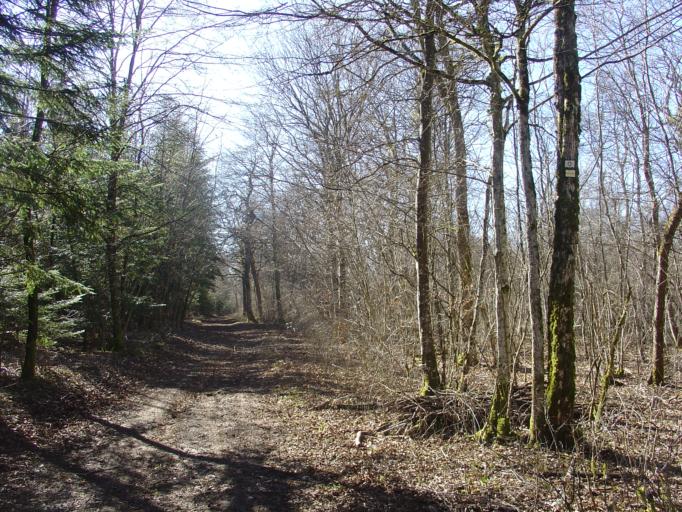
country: FR
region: Lorraine
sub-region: Departement de Meurthe-et-Moselle
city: Blenod-les-Toul
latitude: 48.5812
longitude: 5.8340
